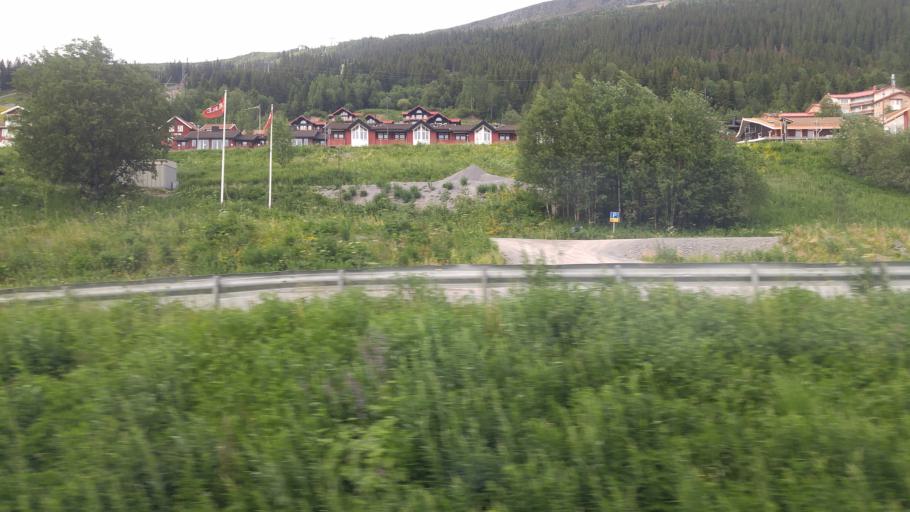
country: SE
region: Jaemtland
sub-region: Are Kommun
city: Are
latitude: 63.4027
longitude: 13.0612
